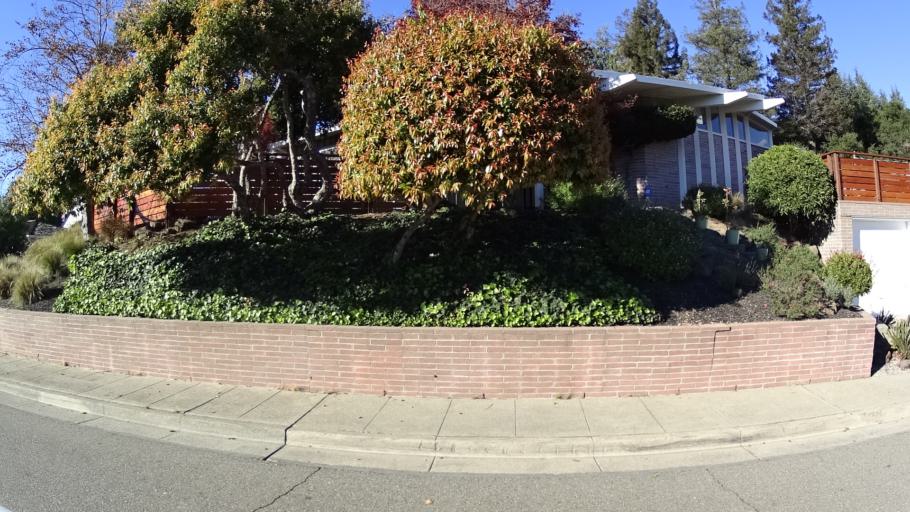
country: US
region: California
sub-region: Alameda County
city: Piedmont
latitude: 37.8241
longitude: -122.2227
